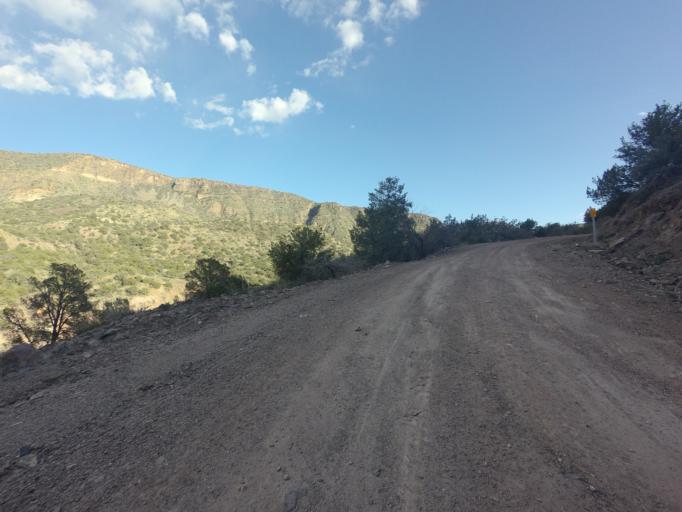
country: US
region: Arizona
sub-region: Gila County
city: Pine
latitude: 34.3789
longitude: -111.6605
